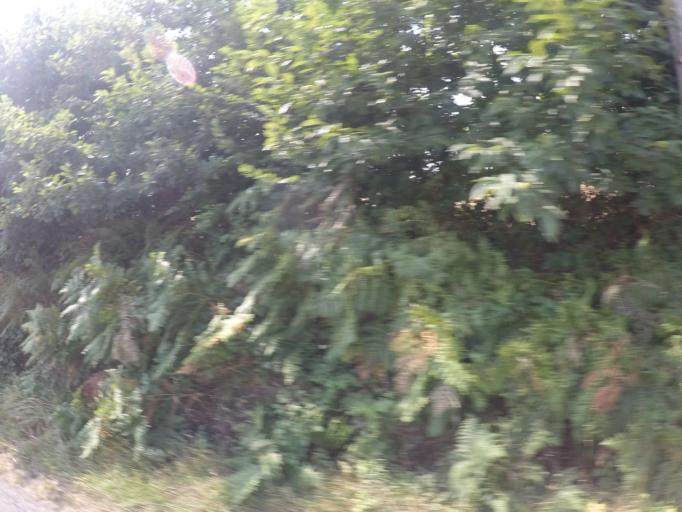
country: FR
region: Brittany
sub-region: Departement des Cotes-d'Armor
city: Tremuson
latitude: 48.5372
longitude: -2.8928
